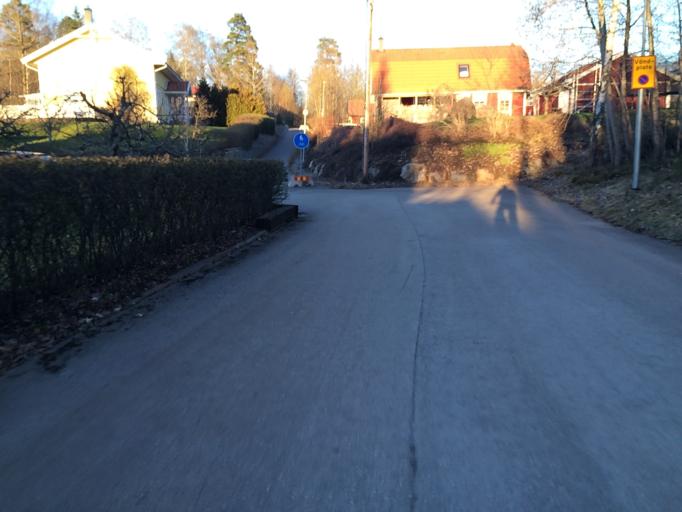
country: SE
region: Soedermanland
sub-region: Eskilstuna Kommun
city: Kvicksund
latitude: 59.4504
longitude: 16.3389
